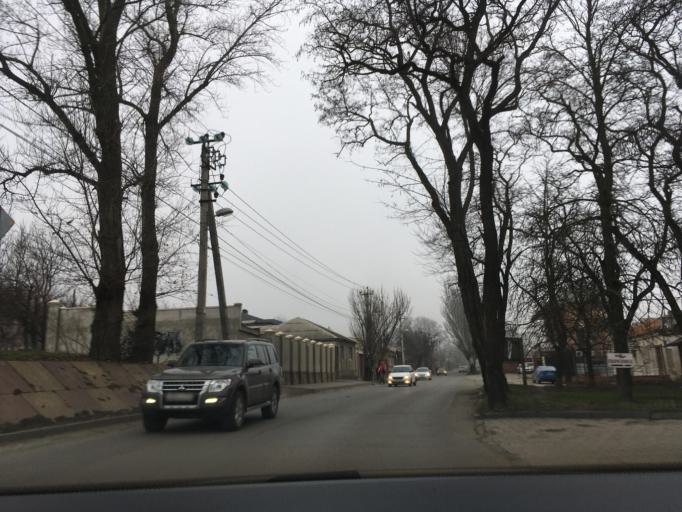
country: RU
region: Rostov
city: Imeni Chkalova
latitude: 47.2368
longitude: 39.7746
